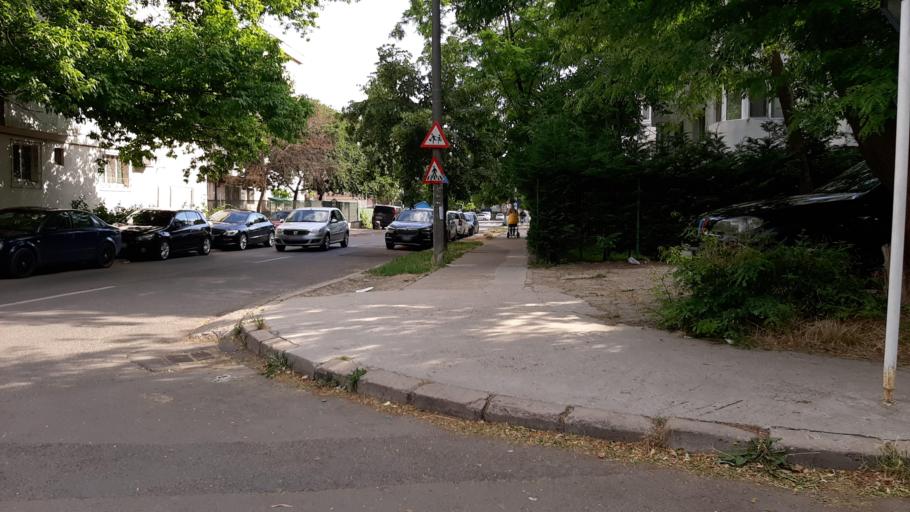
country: RO
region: Galati
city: Galati
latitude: 45.4430
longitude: 28.0270
